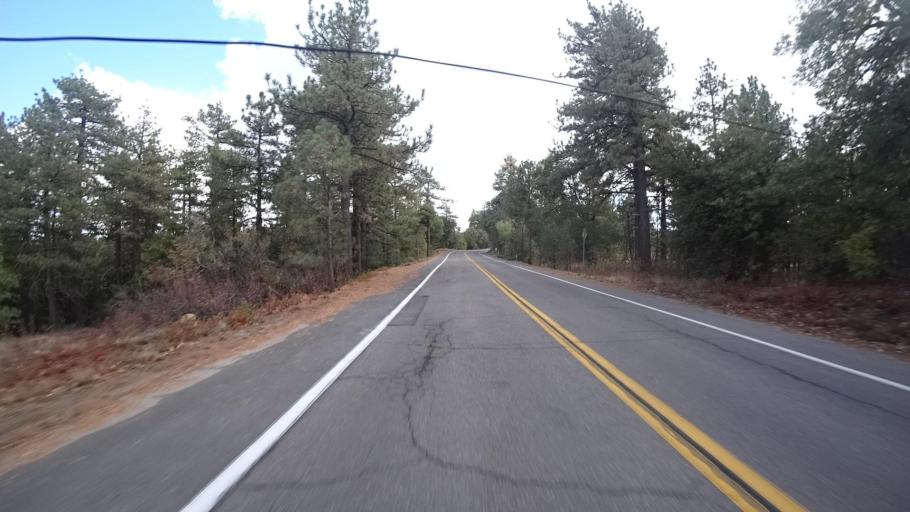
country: US
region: California
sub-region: San Diego County
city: Pine Valley
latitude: 32.8543
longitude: -116.4229
